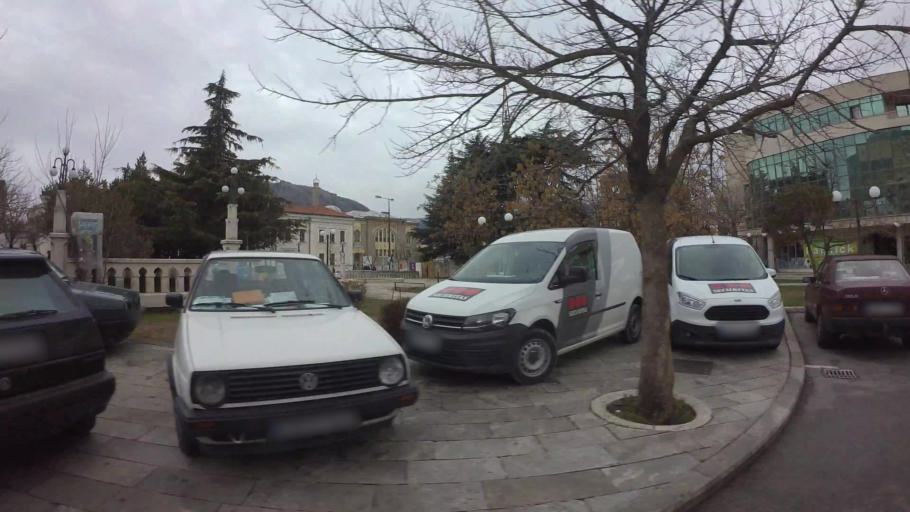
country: BA
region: Federation of Bosnia and Herzegovina
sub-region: Hercegovacko-Bosanski Kanton
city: Mostar
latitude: 43.3448
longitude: 17.8116
